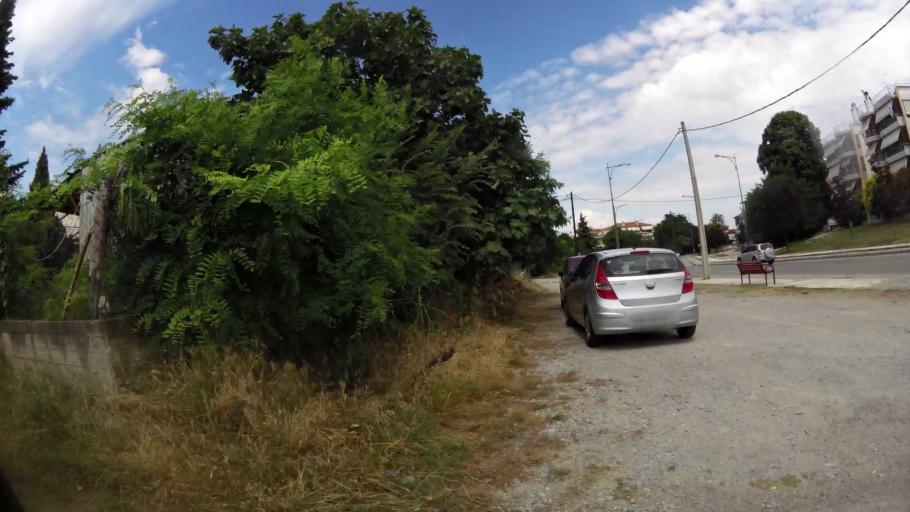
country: GR
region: Central Macedonia
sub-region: Nomos Pierias
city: Katerini
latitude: 40.2773
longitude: 22.5080
